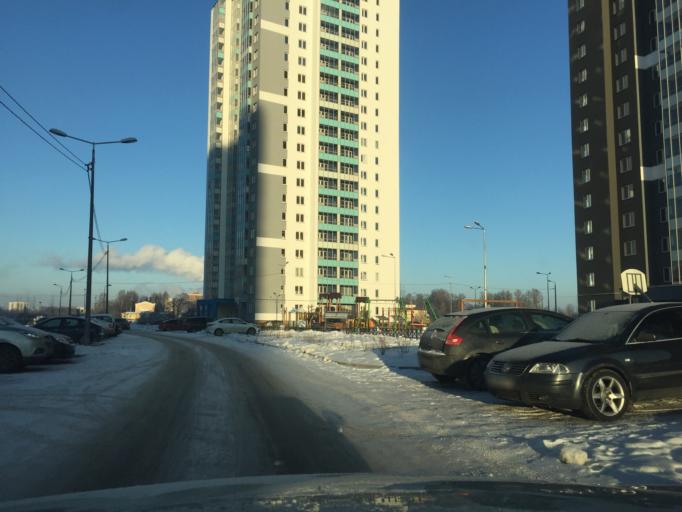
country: RU
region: Leningrad
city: Murino
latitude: 60.0327
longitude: 30.4612
